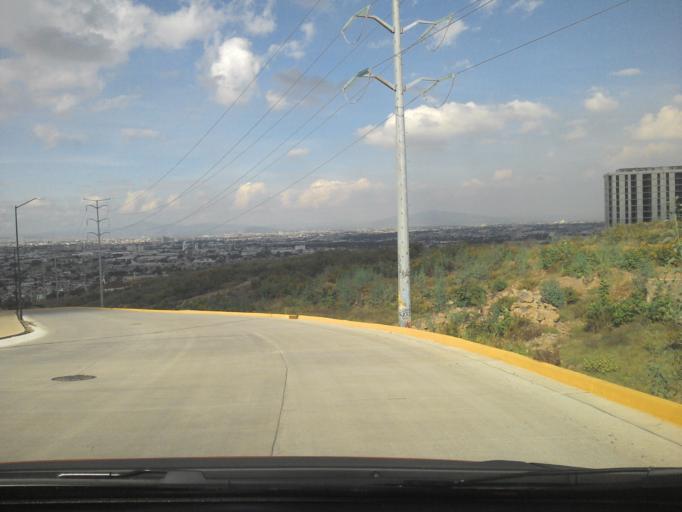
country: MX
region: Jalisco
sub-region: Tlajomulco de Zuniga
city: Altus Bosques
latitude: 20.6086
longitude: -103.3631
